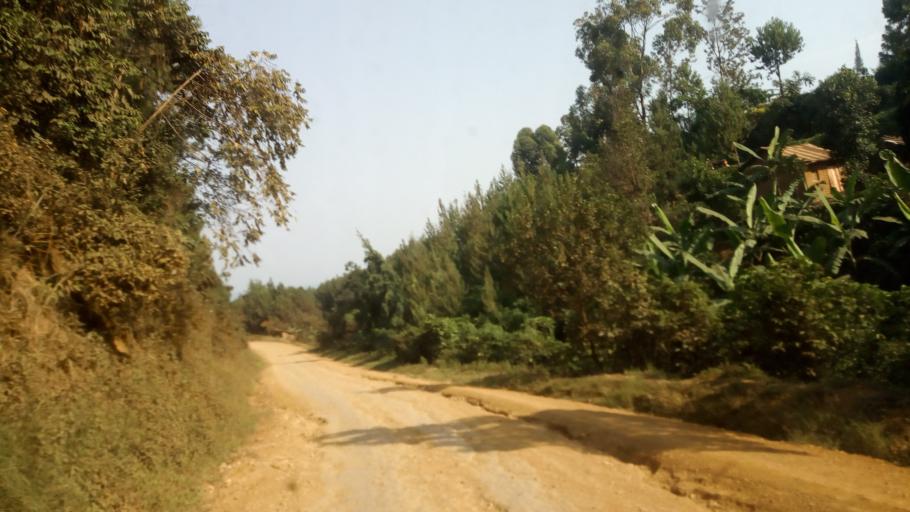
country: UG
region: Western Region
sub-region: Kanungu District
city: Ntungamo
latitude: -0.8275
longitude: 29.7064
